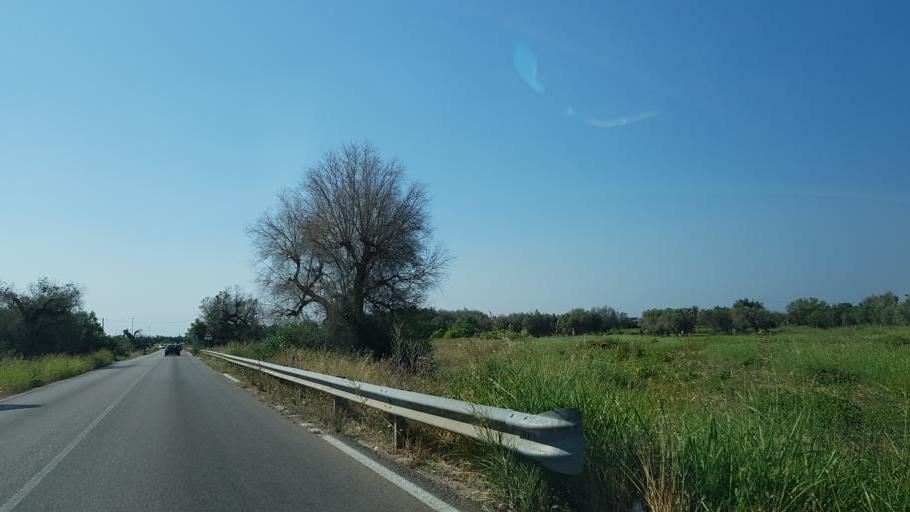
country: IT
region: Apulia
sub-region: Provincia di Lecce
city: Salice Salentino
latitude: 40.4030
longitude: 17.9690
